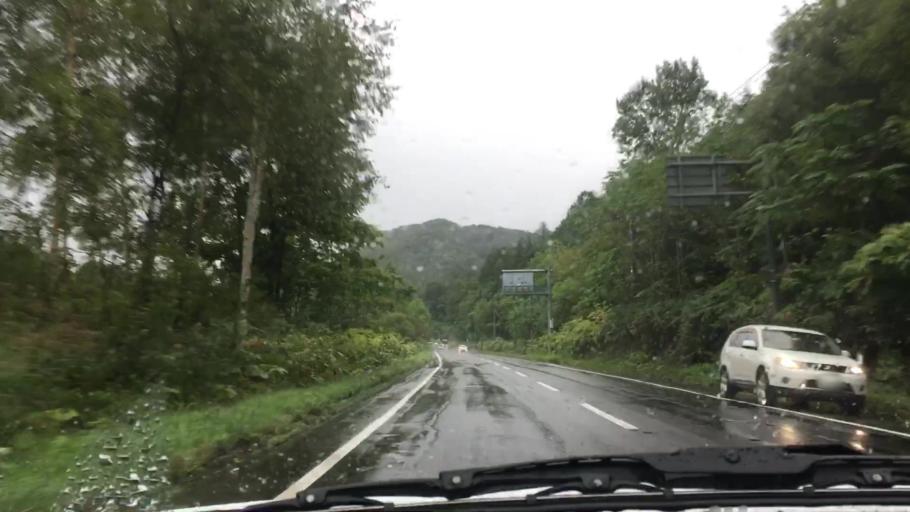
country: JP
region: Hokkaido
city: Niseko Town
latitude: 42.8274
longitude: 141.0063
